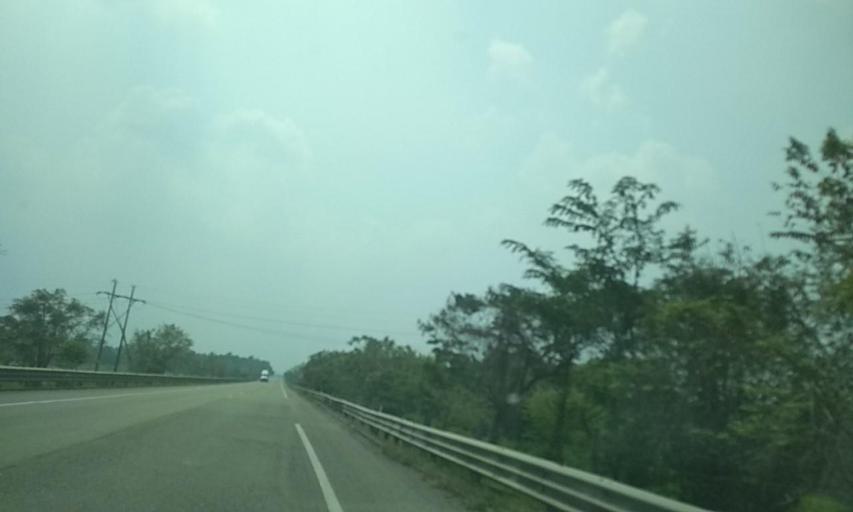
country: MX
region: Tabasco
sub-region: Huimanguillo
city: Francisco Rueda
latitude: 17.7636
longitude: -94.0174
